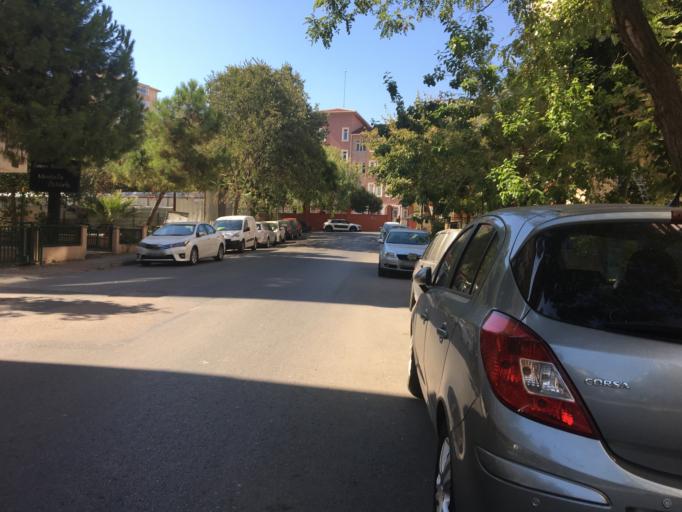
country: TR
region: Istanbul
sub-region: Atasehir
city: Atasehir
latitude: 40.9626
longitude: 29.1004
